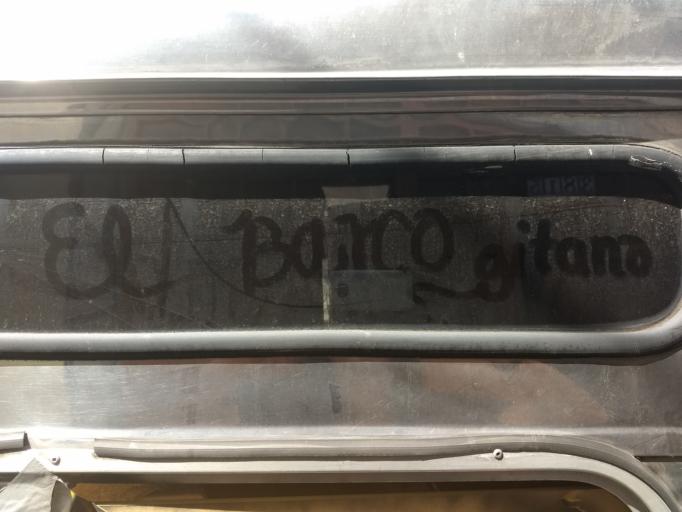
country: MX
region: Mexico City
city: Venustiano Carranza
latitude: 19.4608
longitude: -99.1092
